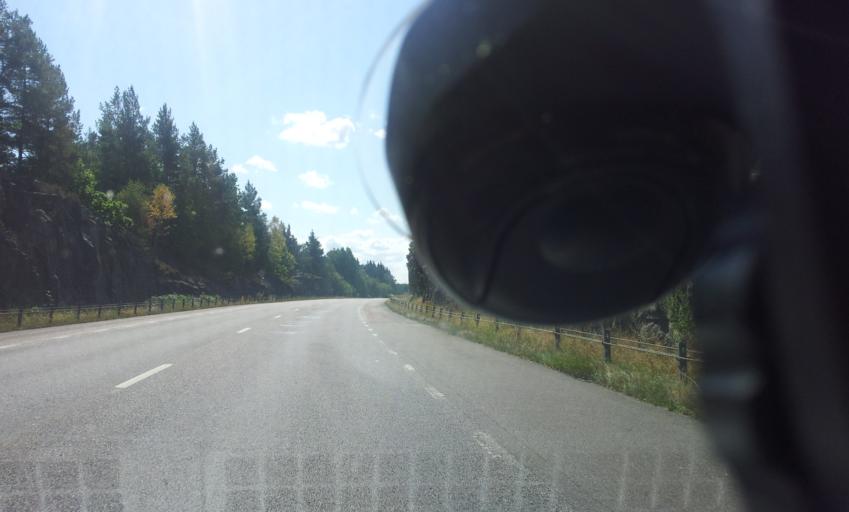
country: SE
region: Kalmar
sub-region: Vasterviks Kommun
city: Ankarsrum
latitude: 57.6484
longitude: 16.4428
